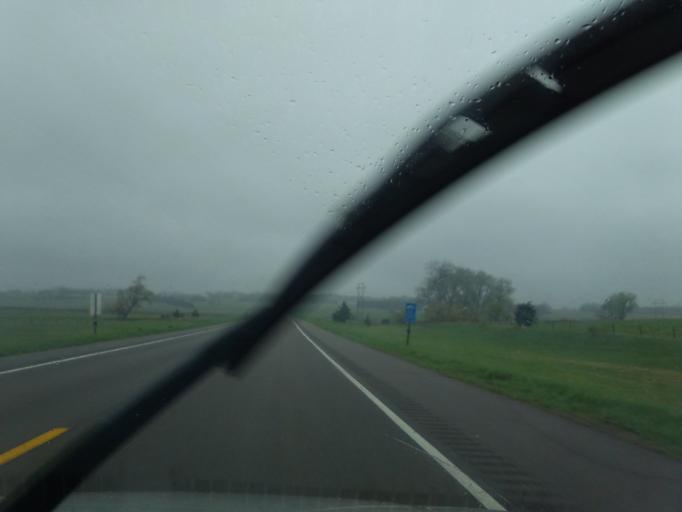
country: US
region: Nebraska
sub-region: Madison County
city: Norfolk
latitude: 42.0867
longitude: -97.3231
